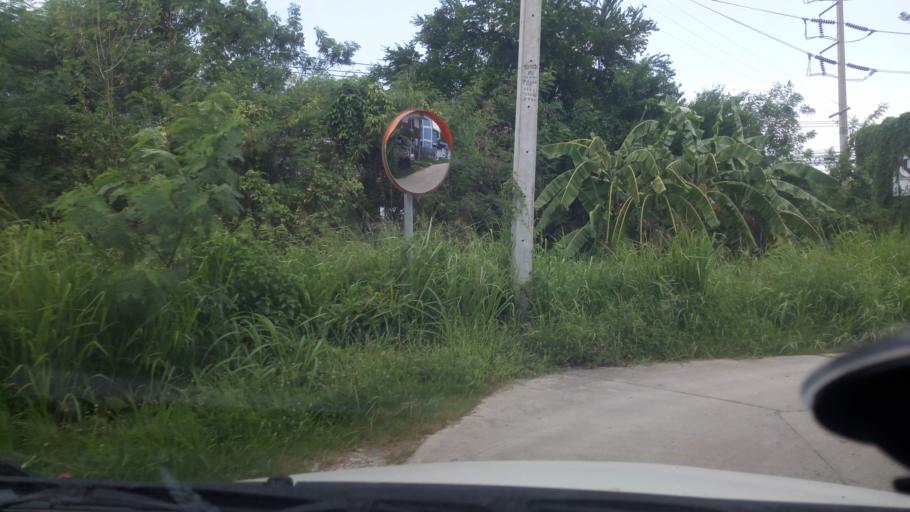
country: TH
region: Chon Buri
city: Phan Thong
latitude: 13.4104
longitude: 101.0517
